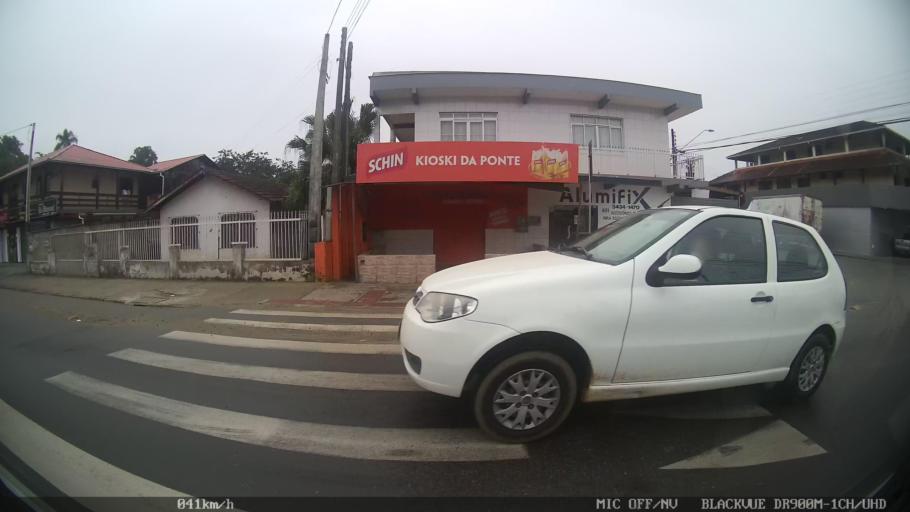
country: BR
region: Santa Catarina
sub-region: Joinville
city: Joinville
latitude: -26.2753
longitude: -48.8055
